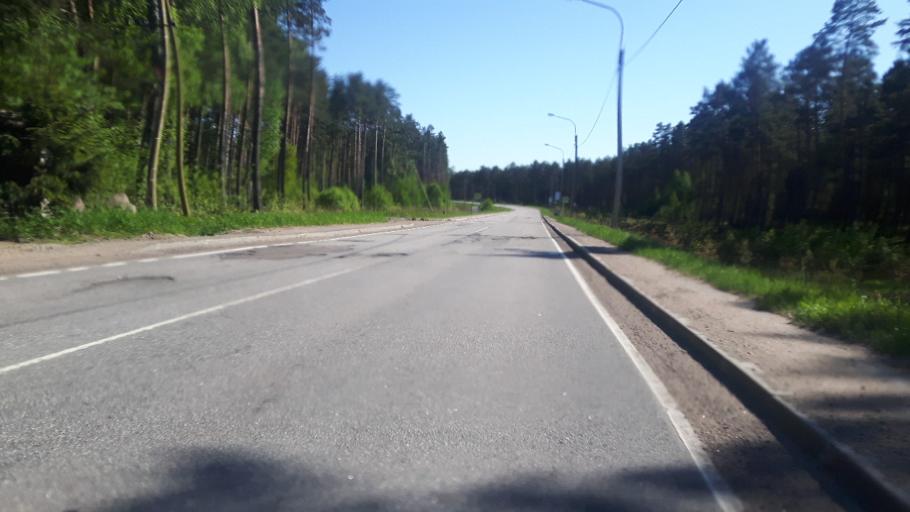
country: RU
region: Leningrad
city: Sosnovyy Bor
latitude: 60.2080
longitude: 29.0060
